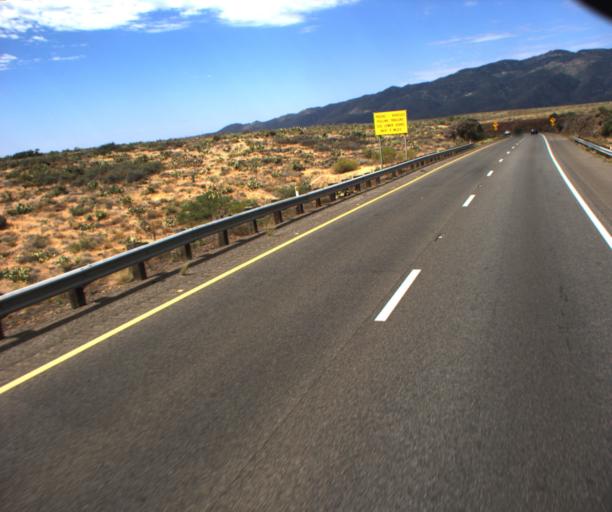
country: US
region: Arizona
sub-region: Yavapai County
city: Black Canyon City
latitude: 34.1723
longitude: -112.1392
